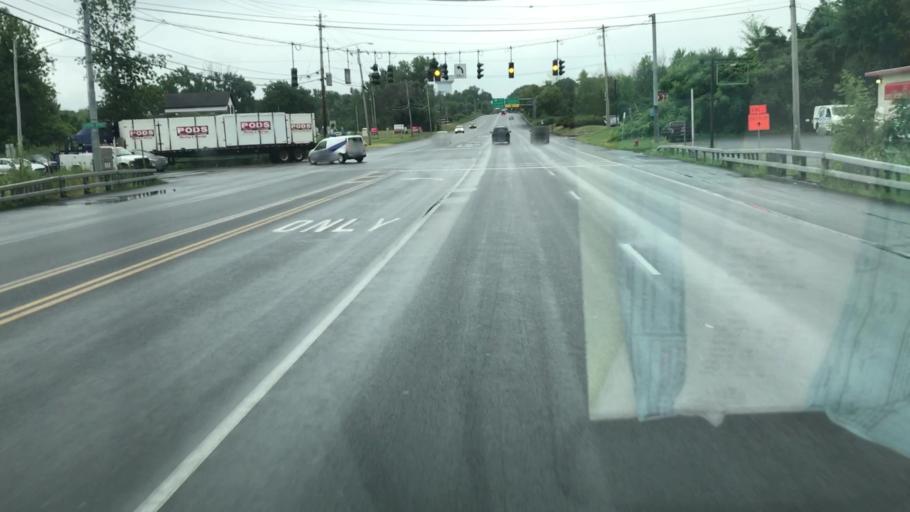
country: US
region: New York
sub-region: Onondaga County
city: Liverpool
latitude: 43.1201
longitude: -76.2153
